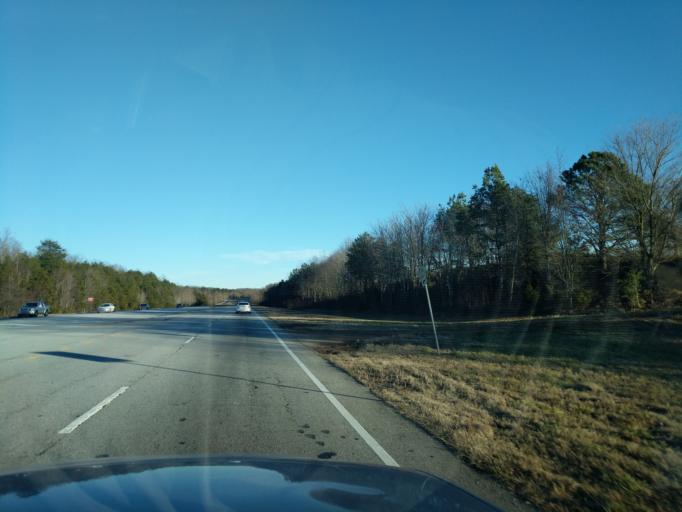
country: US
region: Georgia
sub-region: Habersham County
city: Clarkesville
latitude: 34.5945
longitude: -83.4296
